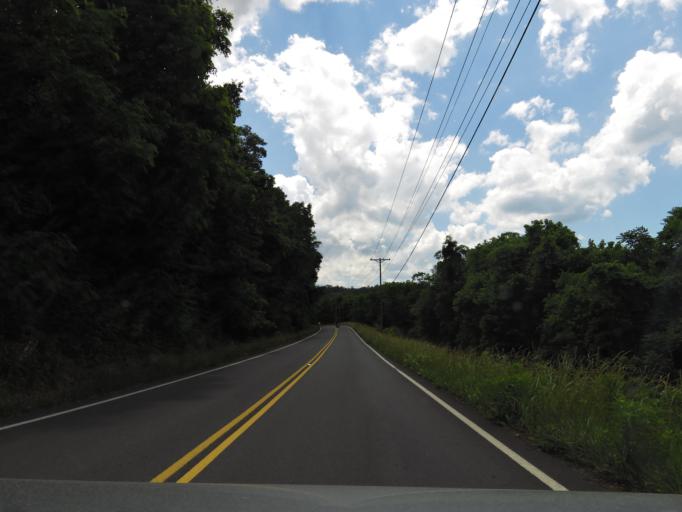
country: US
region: Tennessee
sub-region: Loudon County
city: Greenback
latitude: 35.5442
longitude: -84.0868
